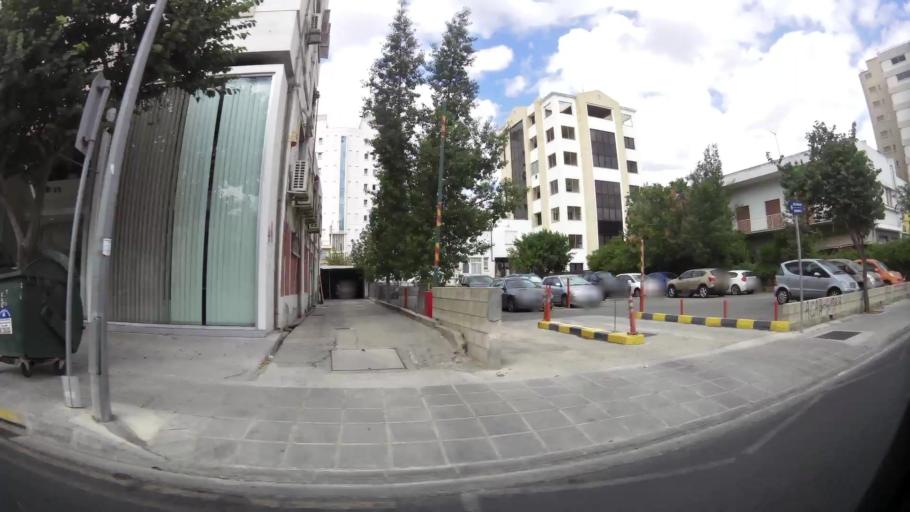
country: CY
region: Lefkosia
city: Nicosia
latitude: 35.1655
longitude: 33.3680
